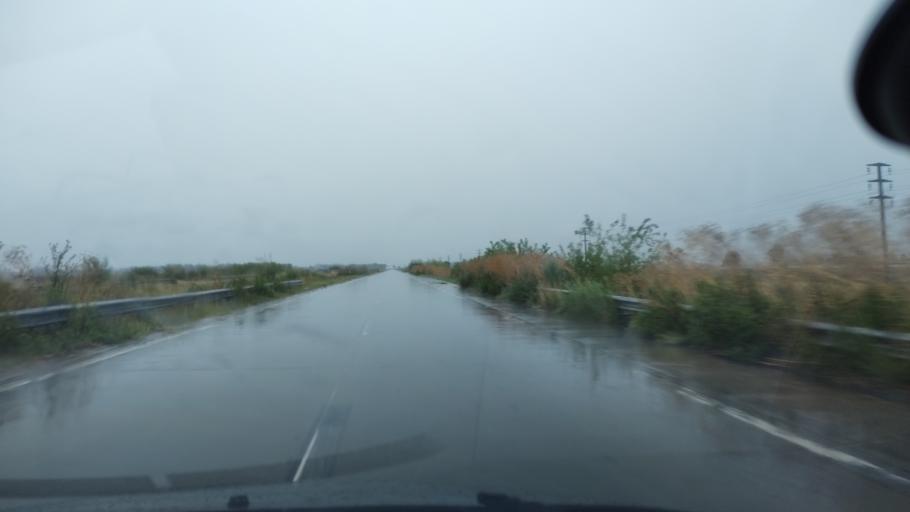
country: AR
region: Buenos Aires
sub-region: Partido de San Vicente
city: San Vicente
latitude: -35.0632
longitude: -58.4699
